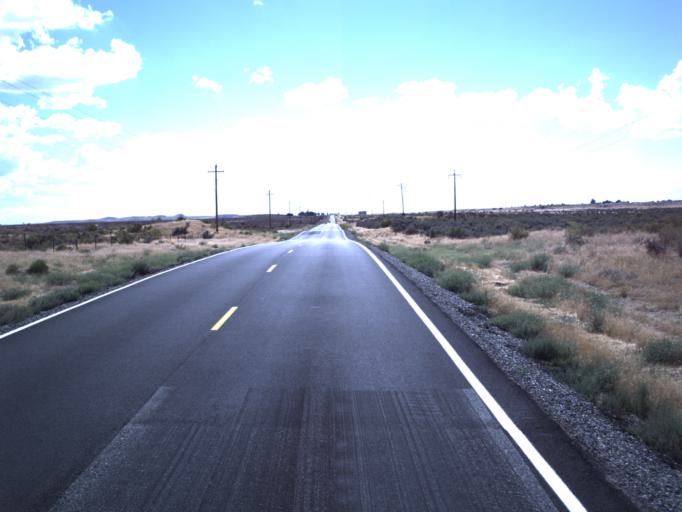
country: US
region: Utah
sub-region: Tooele County
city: Grantsville
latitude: 40.2462
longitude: -112.7080
